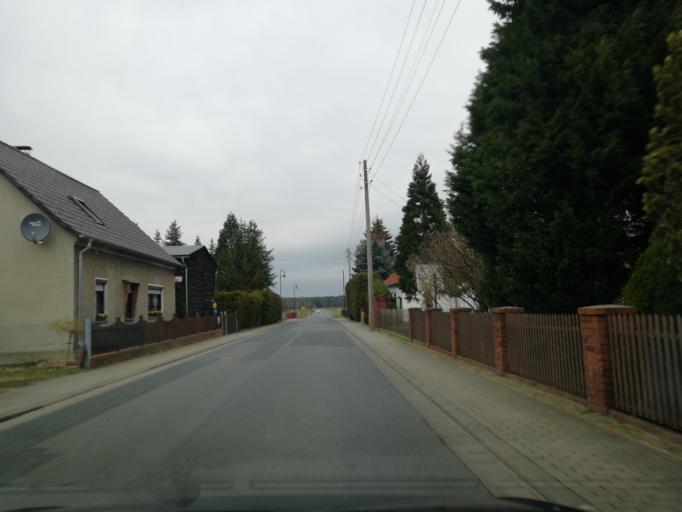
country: DE
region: Brandenburg
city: Vetschau
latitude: 51.7287
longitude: 14.0534
